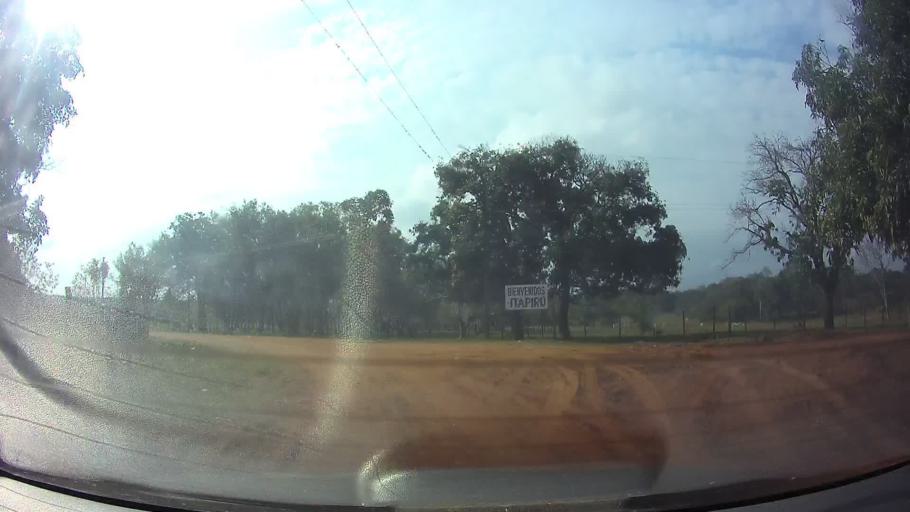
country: PY
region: Cordillera
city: Arroyos y Esteros
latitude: -25.0100
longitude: -57.1983
